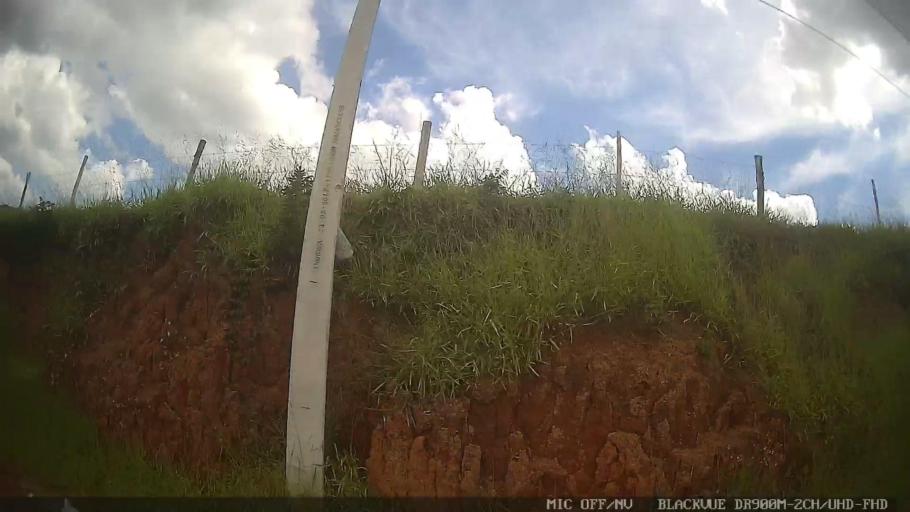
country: BR
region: Minas Gerais
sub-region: Extrema
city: Extrema
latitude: -22.8476
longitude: -46.2721
